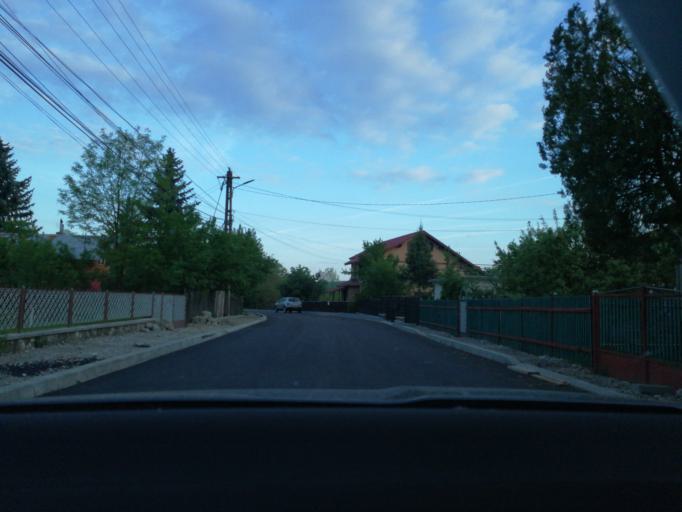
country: RO
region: Prahova
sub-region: Comuna Cornu
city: Cornu de Jos
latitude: 45.1464
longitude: 25.7024
